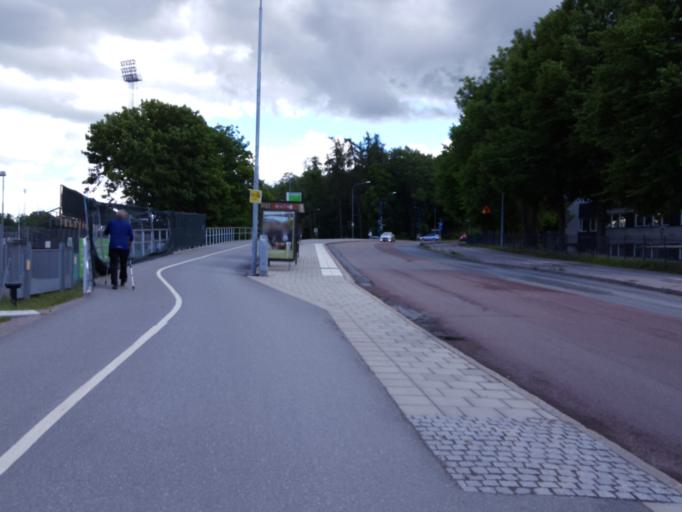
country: SE
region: Uppsala
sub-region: Uppsala Kommun
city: Uppsala
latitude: 59.8500
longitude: 17.6436
